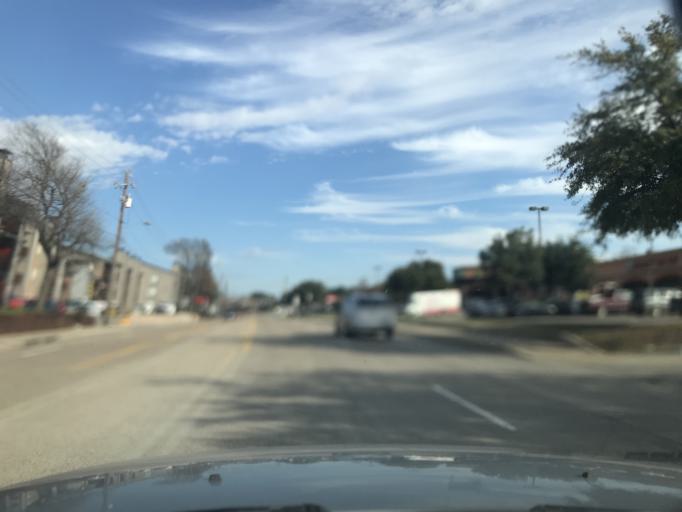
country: US
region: Texas
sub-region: Dallas County
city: Addison
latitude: 33.0105
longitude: -96.8466
